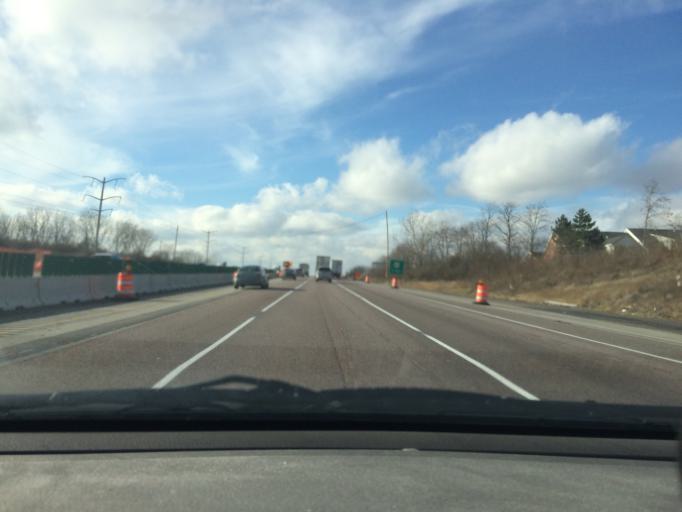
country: US
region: Illinois
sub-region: Cook County
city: Streamwood
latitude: 42.0666
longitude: -88.1652
